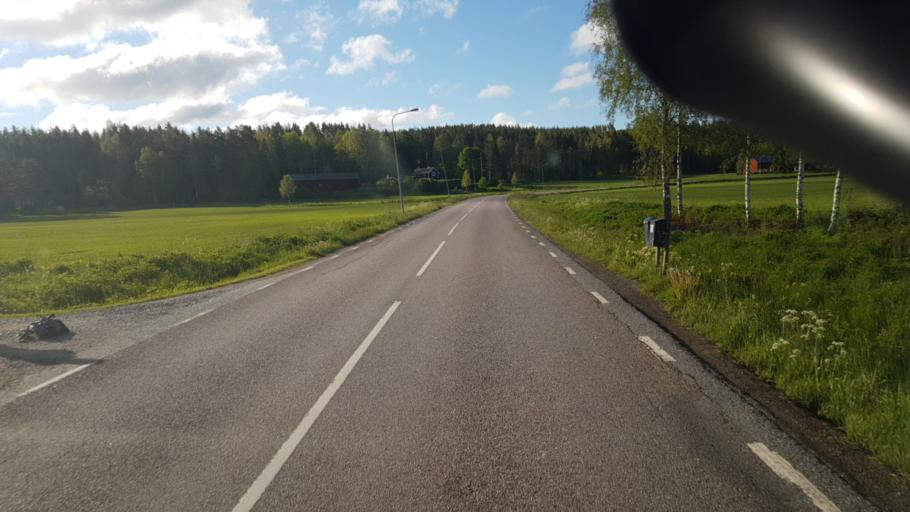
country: SE
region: Vaermland
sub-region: Arvika Kommun
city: Arvika
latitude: 59.5723
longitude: 12.5556
